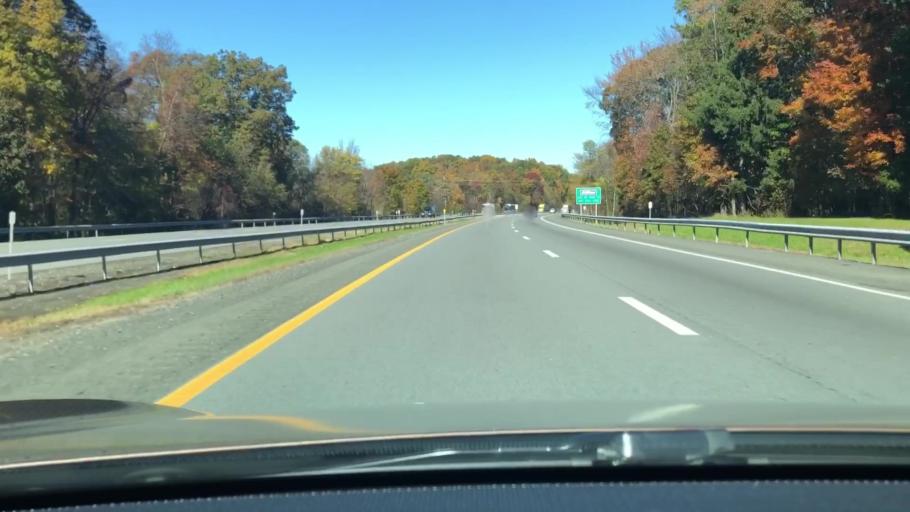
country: US
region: New York
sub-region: Orange County
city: Vails Gate
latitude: 41.4837
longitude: -74.0794
